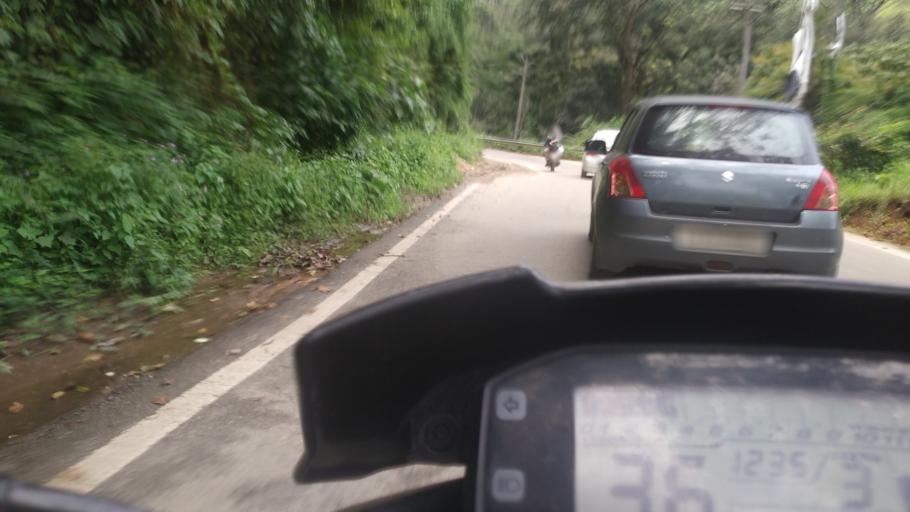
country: IN
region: Kerala
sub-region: Idukki
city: Munnar
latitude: 10.0389
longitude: 77.0325
